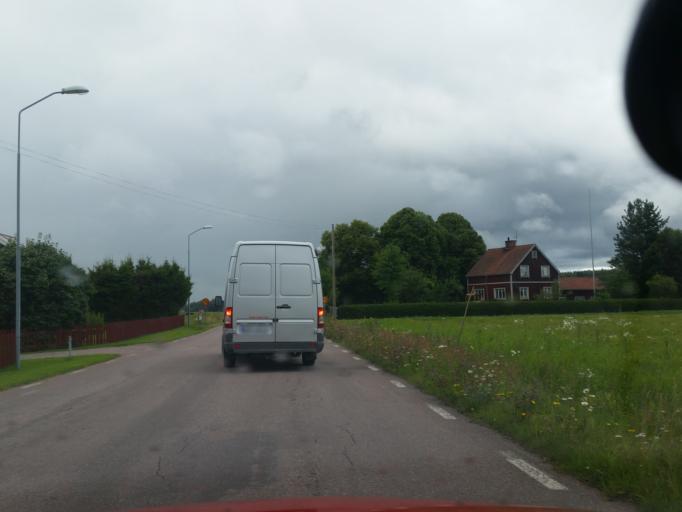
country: SE
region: Dalarna
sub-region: Leksand Municipality
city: Smedby
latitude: 60.7049
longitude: 15.0414
